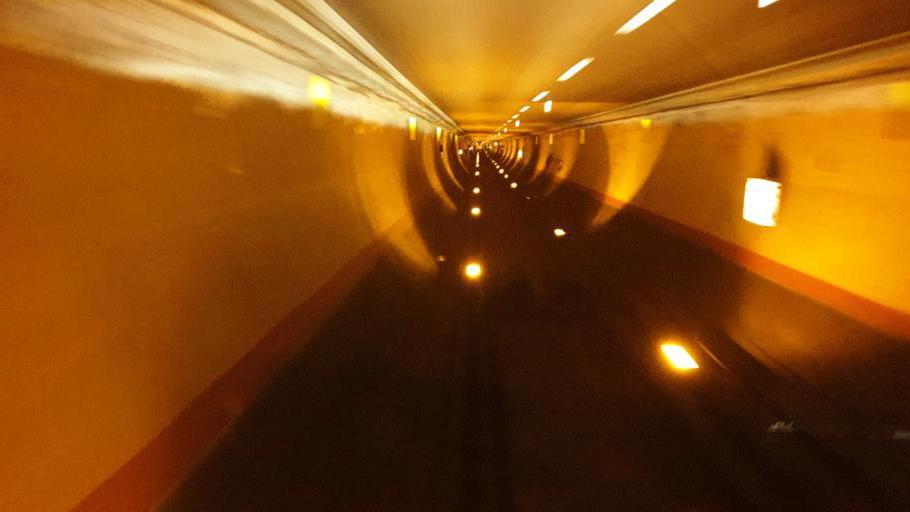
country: IT
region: Emilia-Romagna
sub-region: Forli-Cesena
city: Sarsina
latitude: 43.8986
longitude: 12.0965
